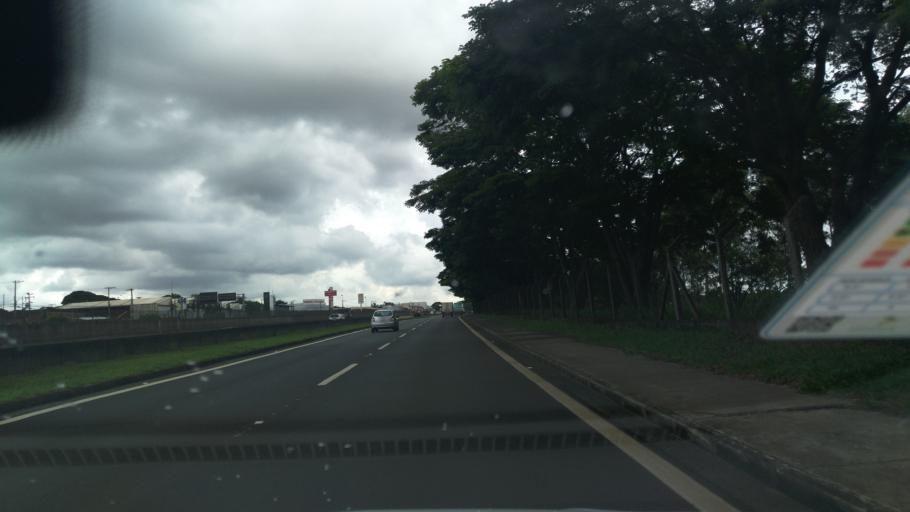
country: BR
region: Sao Paulo
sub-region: Campinas
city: Campinas
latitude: -22.8845
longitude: -47.1149
